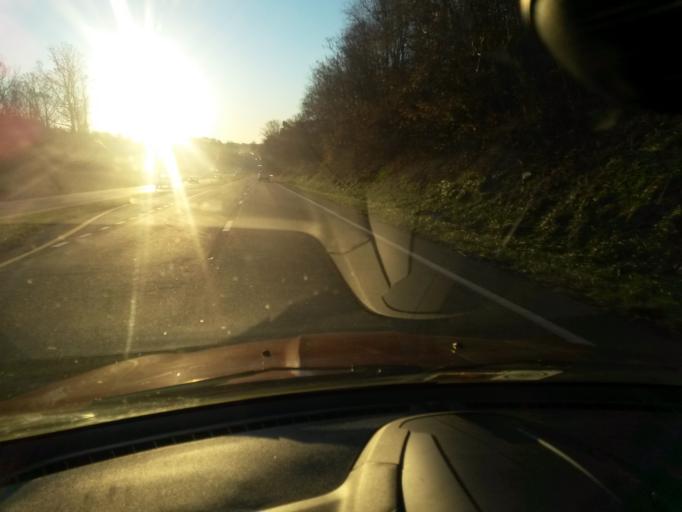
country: US
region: Virginia
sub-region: Franklin County
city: Rocky Mount
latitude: 37.0834
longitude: -79.9258
